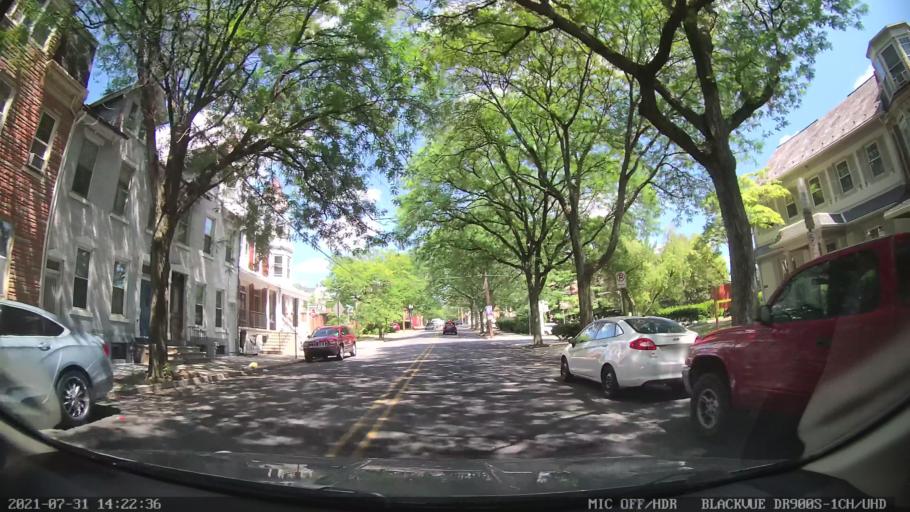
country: US
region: Pennsylvania
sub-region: Lehigh County
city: Allentown
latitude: 40.5986
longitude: -75.4787
